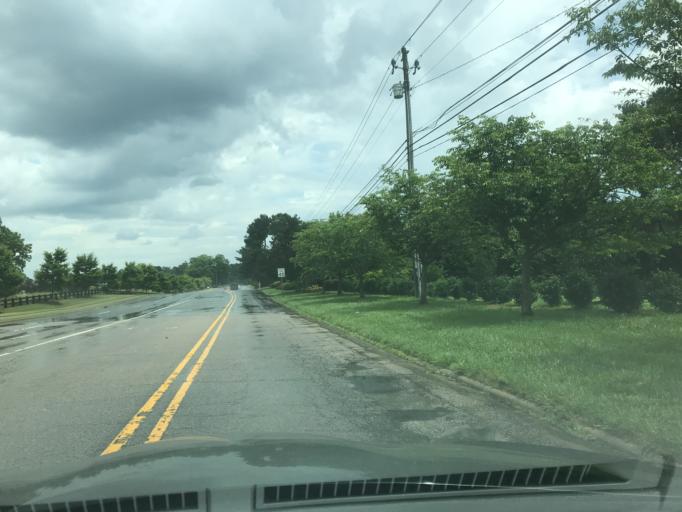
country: US
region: North Carolina
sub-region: Wake County
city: Knightdale
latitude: 35.8340
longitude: -78.5555
